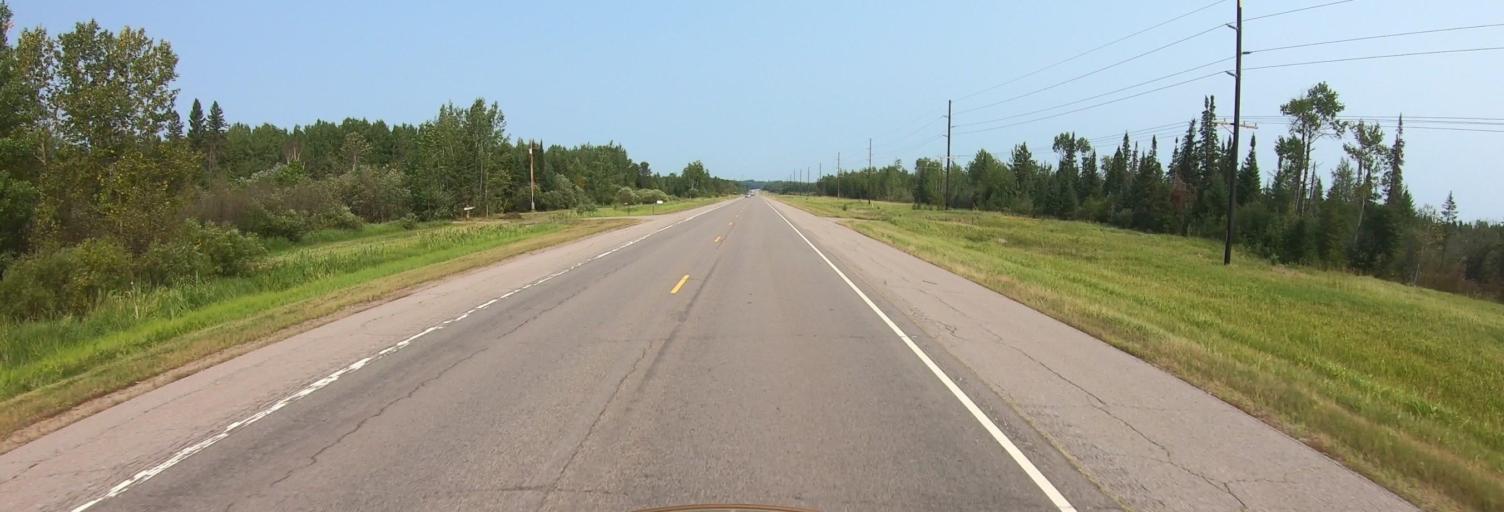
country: US
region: Minnesota
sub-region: Saint Louis County
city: Chisholm
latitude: 47.9339
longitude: -92.8287
